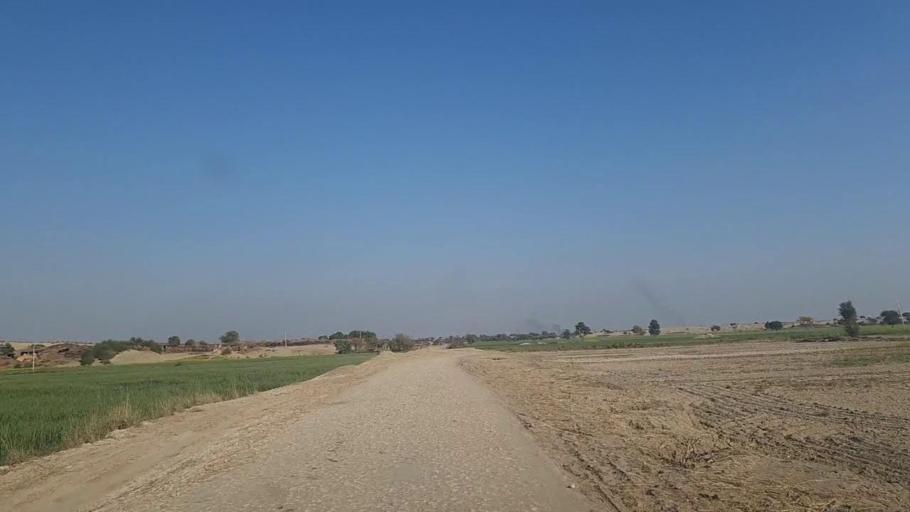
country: PK
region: Sindh
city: Jam Sahib
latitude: 26.3343
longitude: 68.7180
